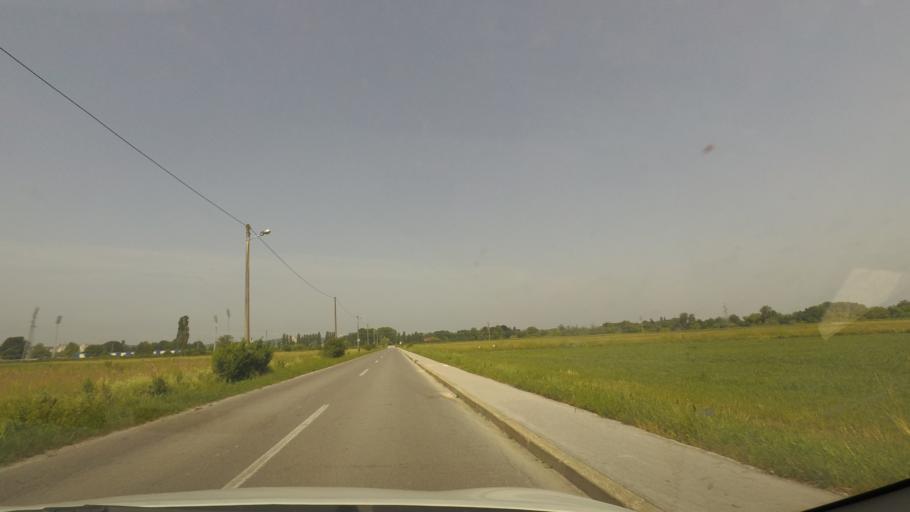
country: HR
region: Karlovacka
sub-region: Grad Karlovac
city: Karlovac
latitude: 45.4848
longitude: 15.5713
